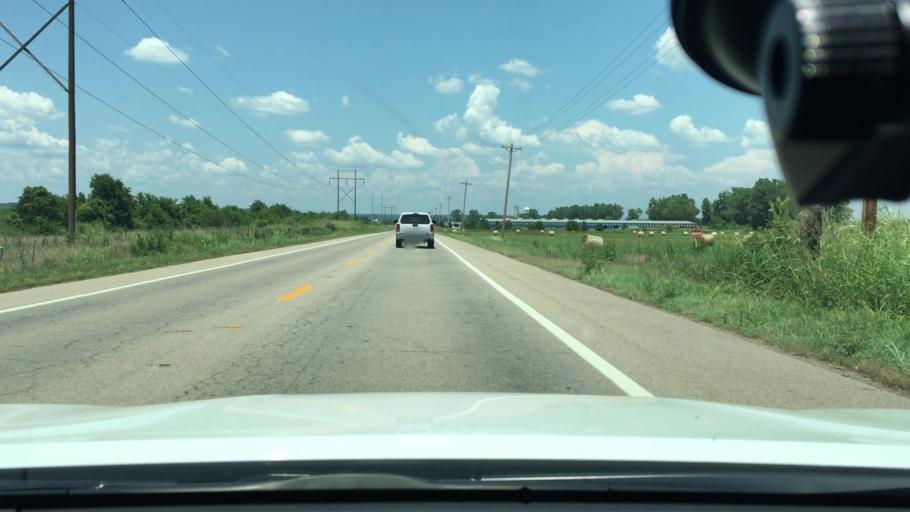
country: US
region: Arkansas
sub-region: Crawford County
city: Van Buren
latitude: 35.3998
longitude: -94.3302
